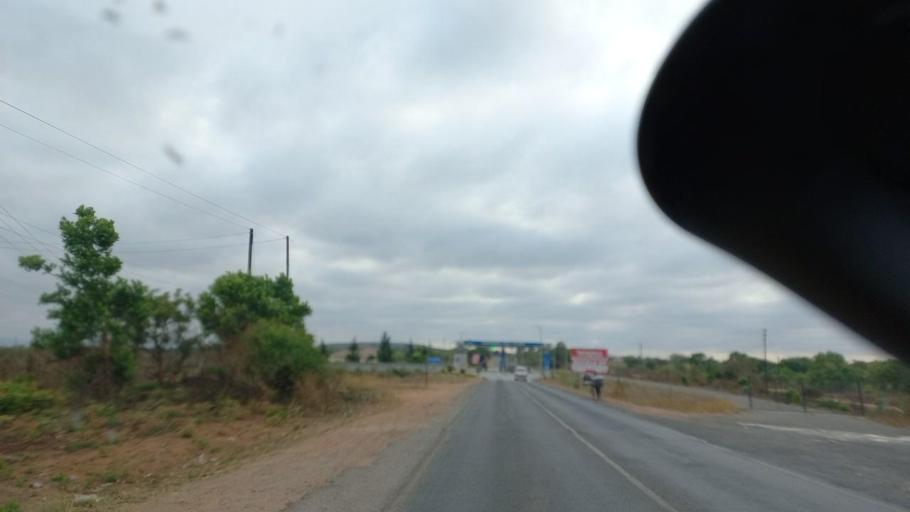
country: ZM
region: Lusaka
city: Chongwe
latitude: -15.3482
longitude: 28.5738
